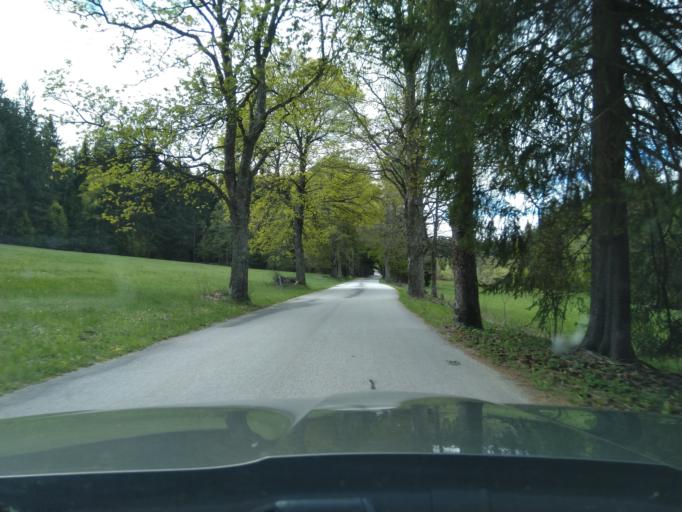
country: CZ
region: Jihocesky
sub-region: Okres Prachatice
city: Vimperk
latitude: 49.0251
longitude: 13.7521
